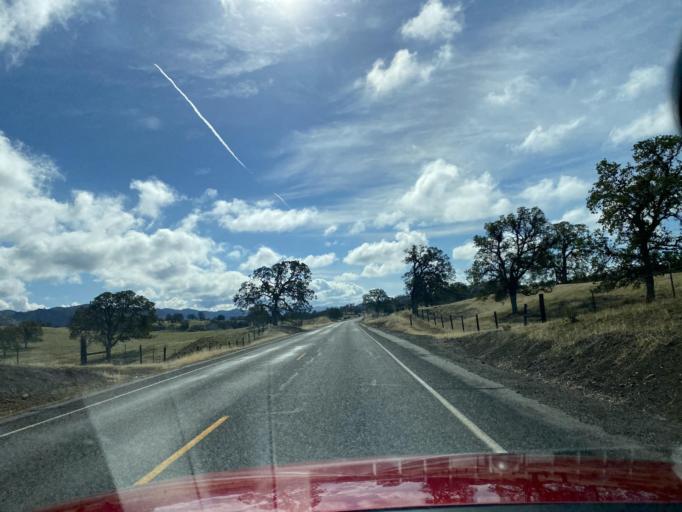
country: US
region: California
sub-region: Glenn County
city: Willows
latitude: 39.5156
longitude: -122.5282
